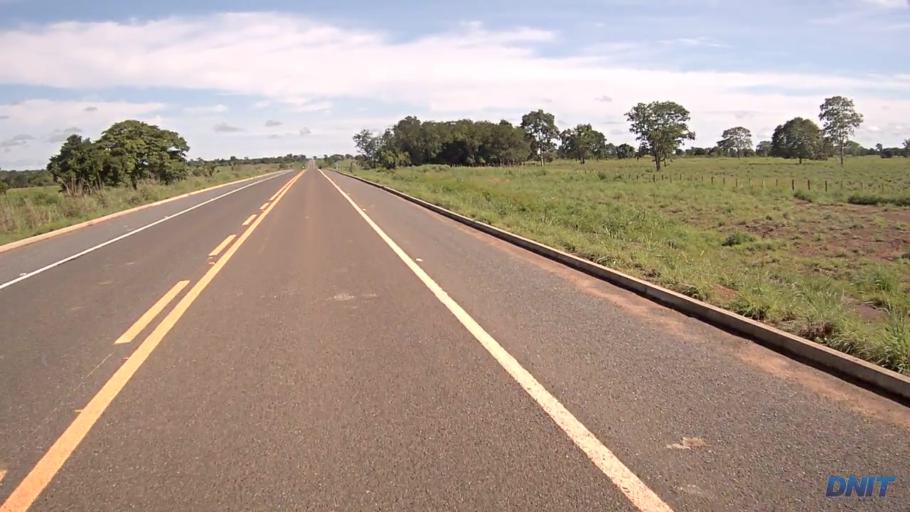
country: BR
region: Goias
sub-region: Sao Miguel Do Araguaia
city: Sao Miguel do Araguaia
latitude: -13.4613
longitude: -50.1176
